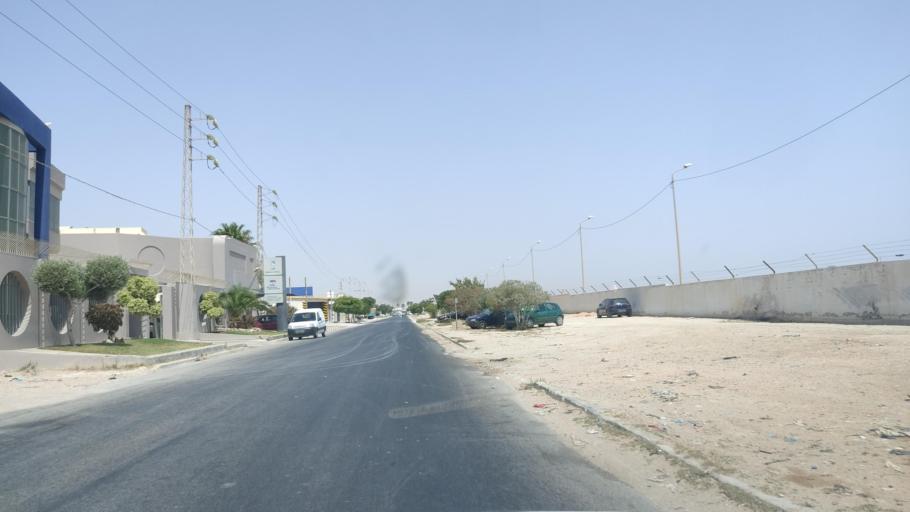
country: TN
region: Safaqis
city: Sfax
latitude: 34.6954
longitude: 10.7232
